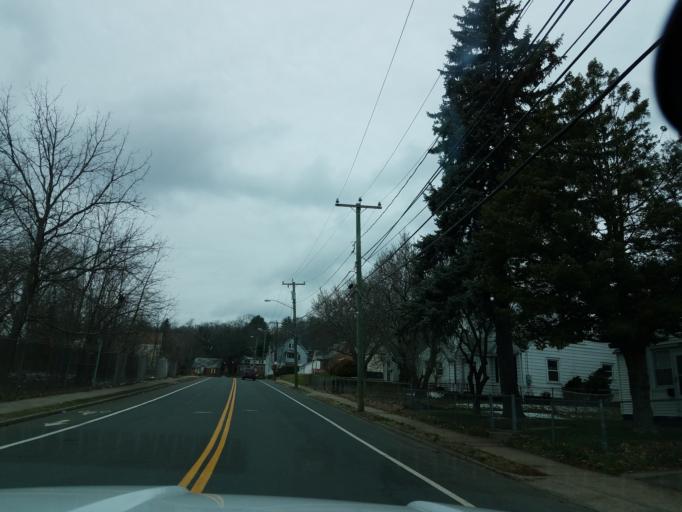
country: US
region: Connecticut
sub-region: Hartford County
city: New Britain
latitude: 41.6704
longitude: -72.8032
